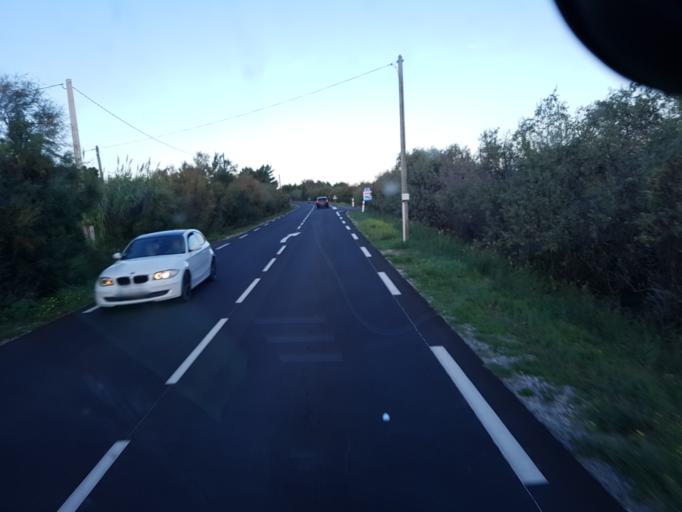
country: FR
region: Languedoc-Roussillon
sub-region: Departement de l'Aude
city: Port-la-Nouvelle
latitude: 42.9849
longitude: 3.0299
